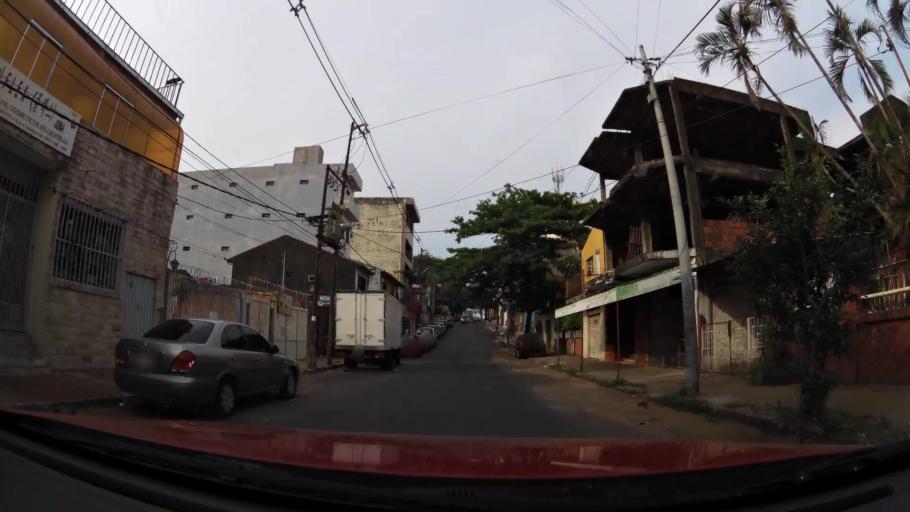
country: PY
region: Asuncion
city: Asuncion
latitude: -25.2965
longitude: -57.6261
